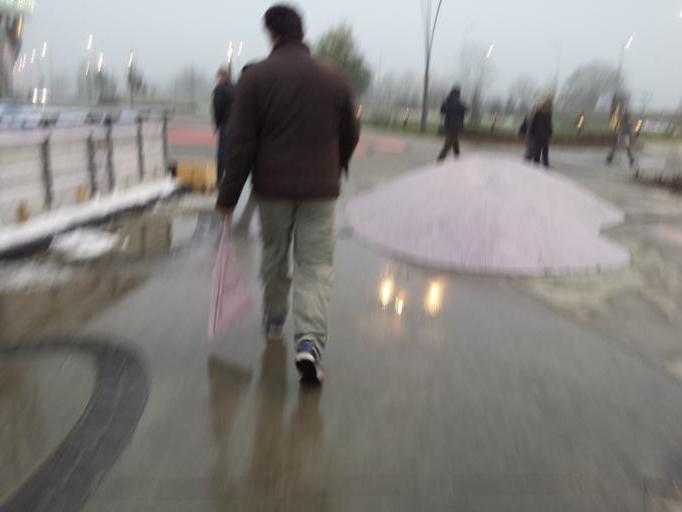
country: HR
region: Grad Zagreb
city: Zadvorsko
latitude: 45.7714
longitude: 15.9401
